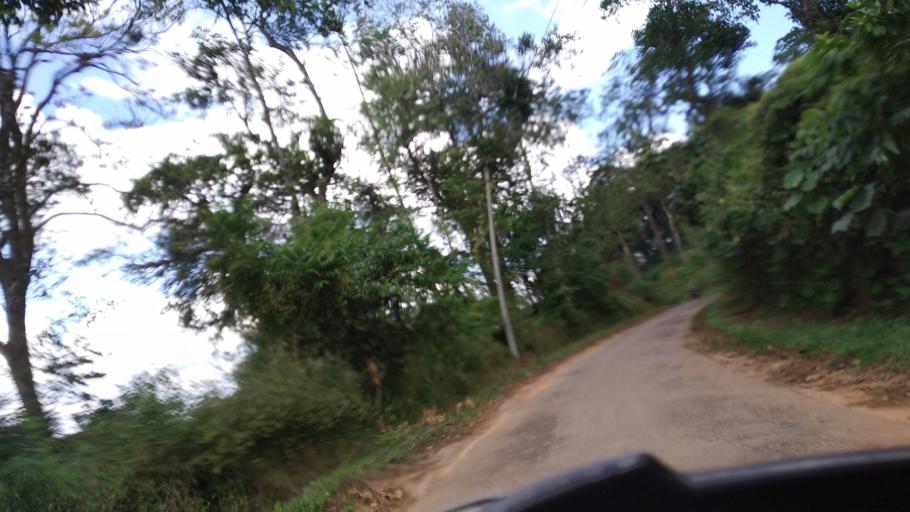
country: IN
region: Karnataka
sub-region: Kodagu
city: Ponnampet
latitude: 12.0368
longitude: 75.9060
